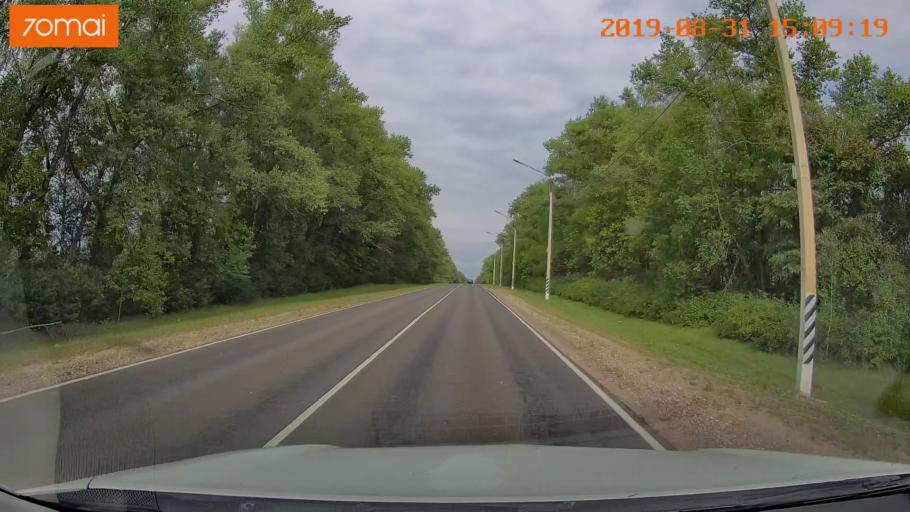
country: RU
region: Kaluga
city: Spas-Demensk
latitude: 54.4005
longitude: 34.1985
